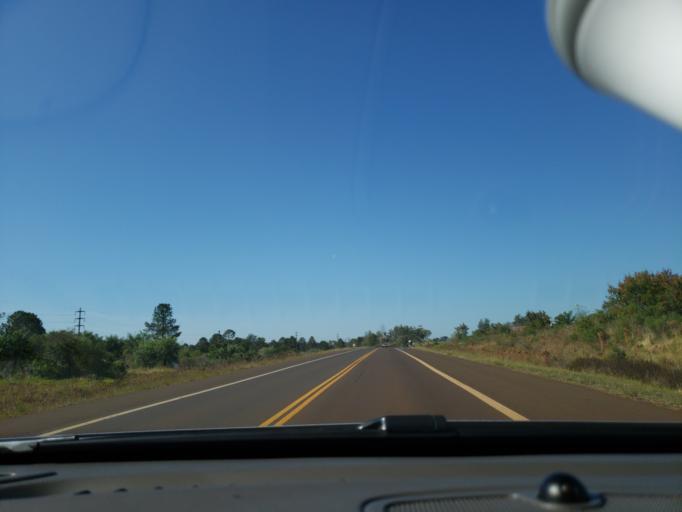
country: AR
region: Misiones
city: Garupa
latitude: -27.4632
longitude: -55.8769
